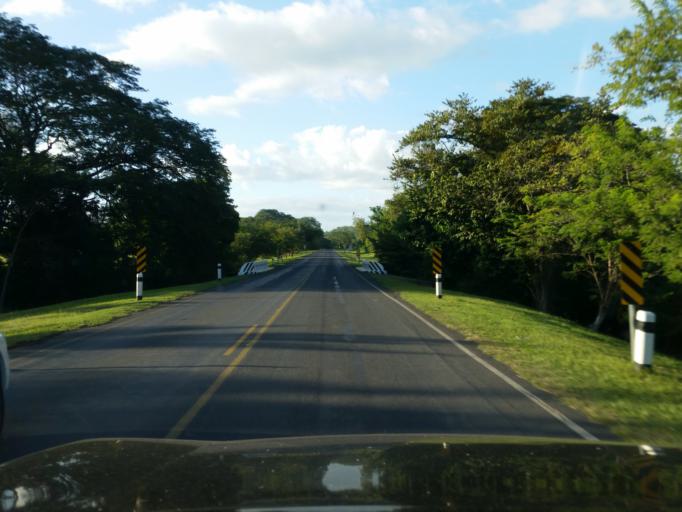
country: NI
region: Granada
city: Nandaime
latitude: 11.7107
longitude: -86.0085
